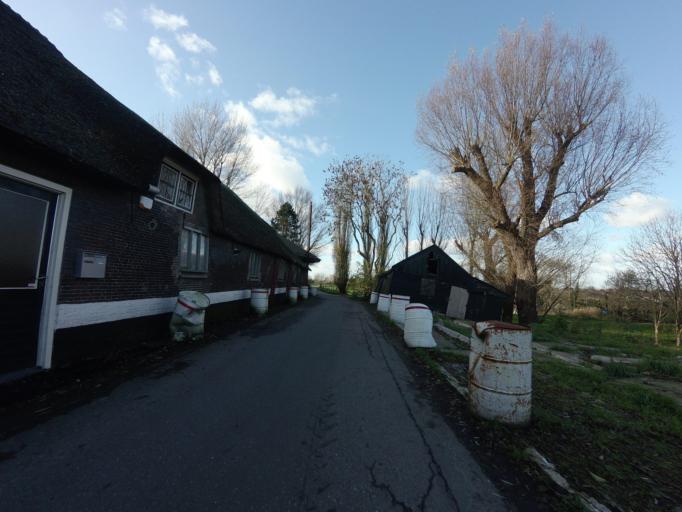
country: NL
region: South Holland
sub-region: Gemeente Kaag en Braassem
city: Leimuiden
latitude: 52.2216
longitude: 4.6869
